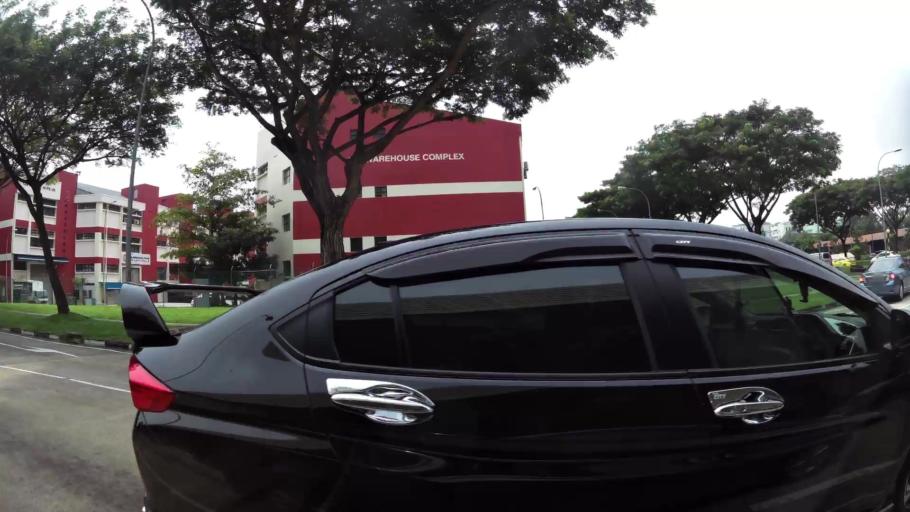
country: SG
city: Singapore
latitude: 1.3400
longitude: 103.8982
